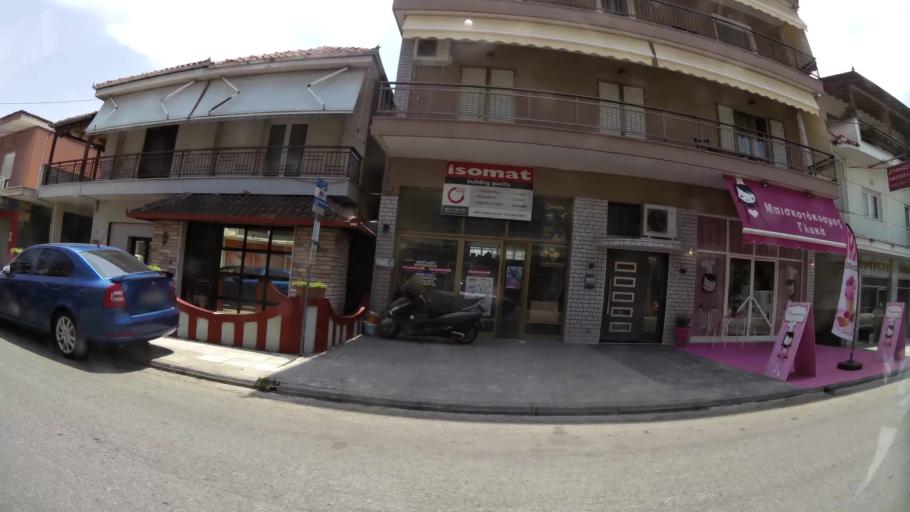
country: GR
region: Central Macedonia
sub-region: Nomos Pierias
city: Peristasi
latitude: 40.2704
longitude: 22.5303
